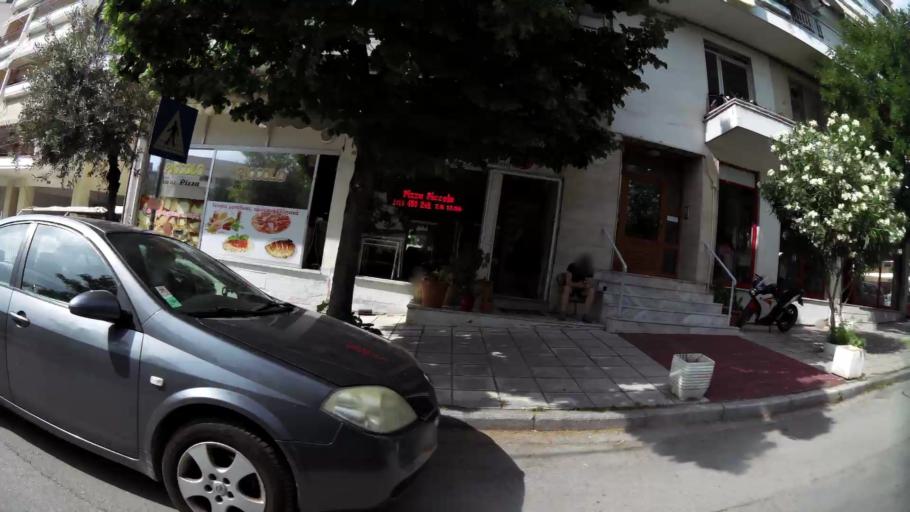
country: GR
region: Central Macedonia
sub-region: Nomos Thessalonikis
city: Kalamaria
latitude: 40.5858
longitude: 22.9657
